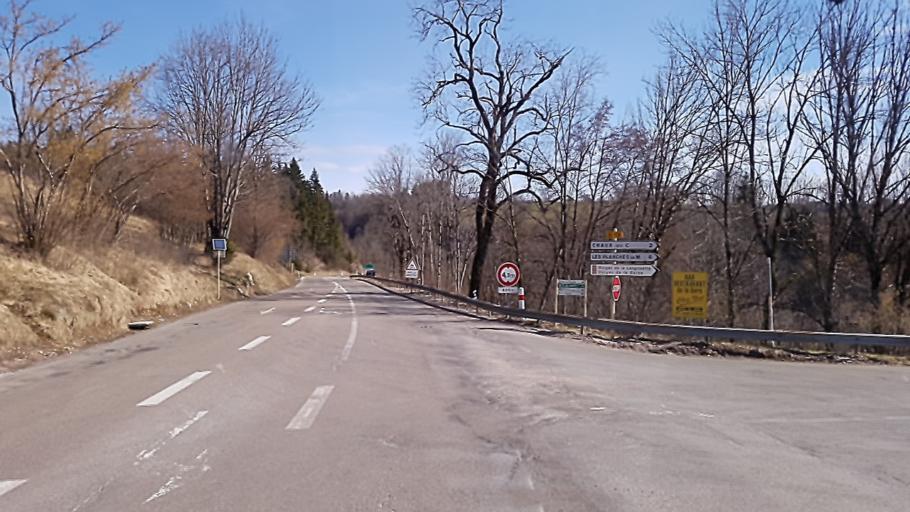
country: FR
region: Franche-Comte
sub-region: Departement du Jura
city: Champagnole
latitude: 46.6560
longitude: 5.9430
